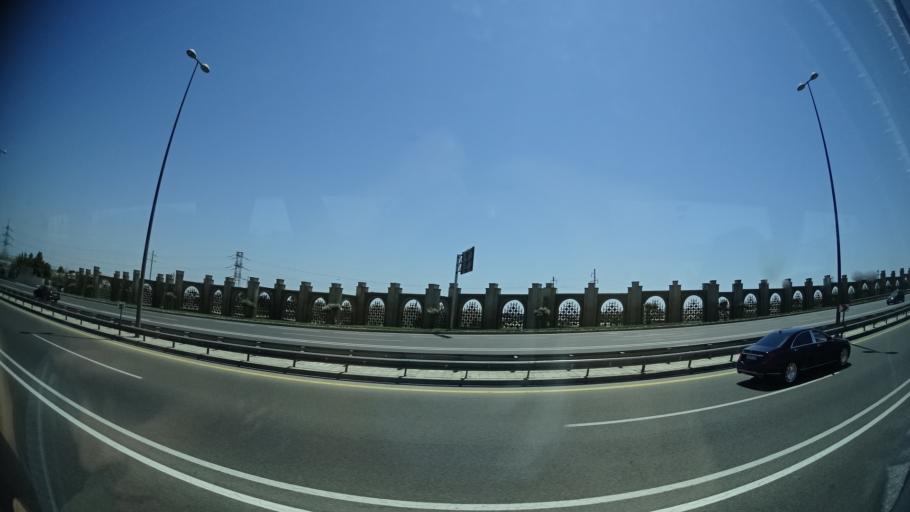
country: AZ
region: Baki
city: Yeni Suraxani
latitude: 40.4358
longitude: 50.0291
